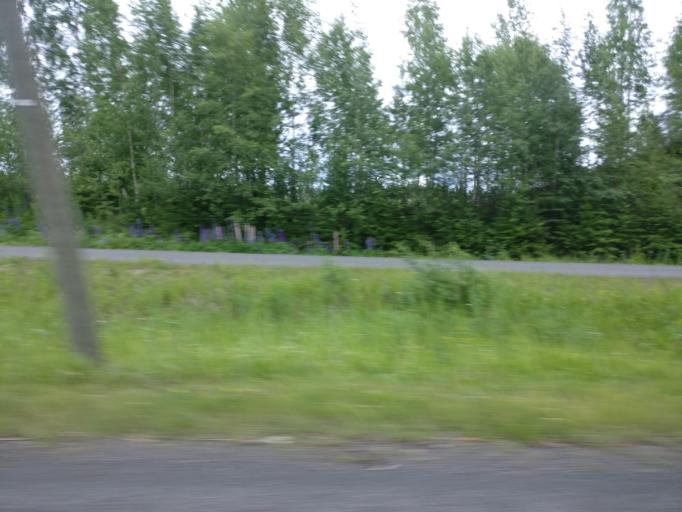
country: FI
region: Northern Savo
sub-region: Varkaus
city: Varkaus
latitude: 62.3435
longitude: 27.8207
